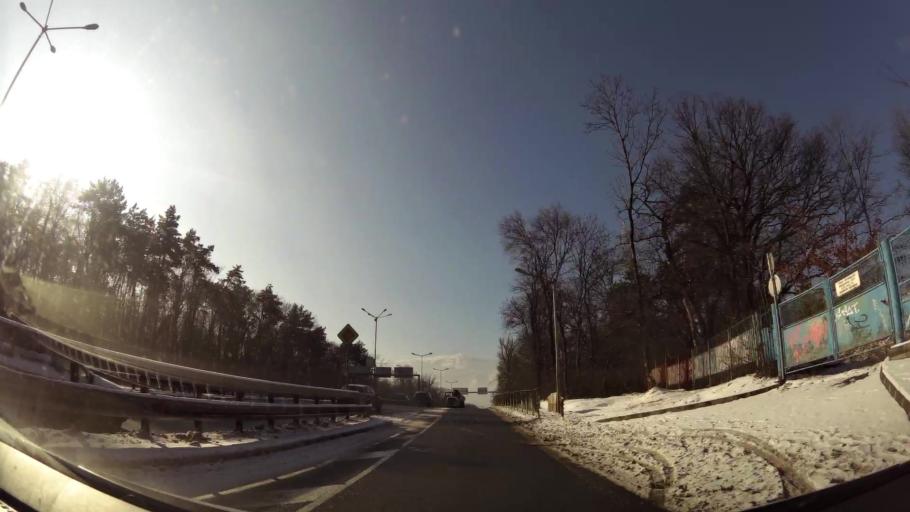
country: BG
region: Sofia-Capital
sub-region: Stolichna Obshtina
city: Sofia
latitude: 42.6759
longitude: 23.3397
